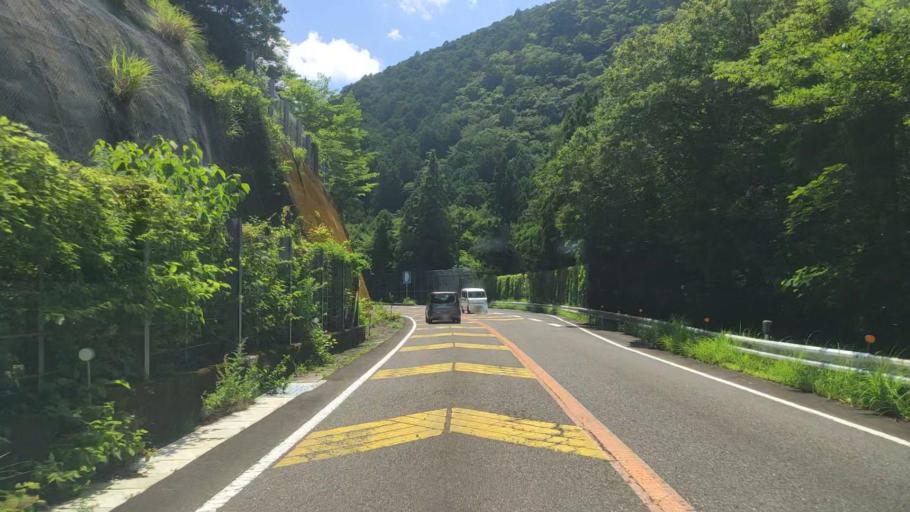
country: JP
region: Mie
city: Owase
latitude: 33.9902
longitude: 136.1130
